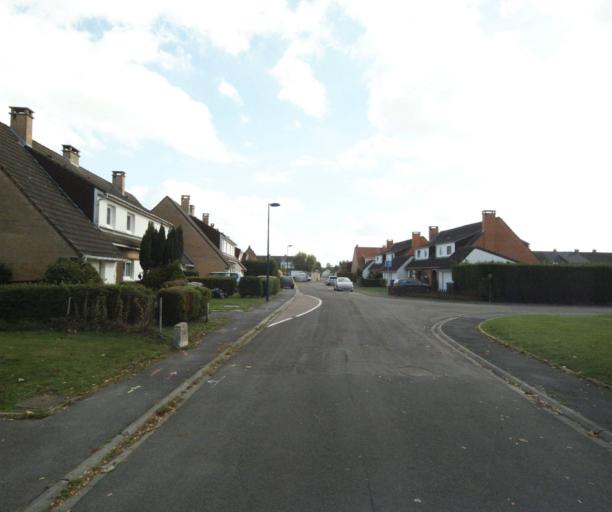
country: FR
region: Nord-Pas-de-Calais
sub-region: Departement du Nord
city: Houplines
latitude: 50.6981
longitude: 2.9181
